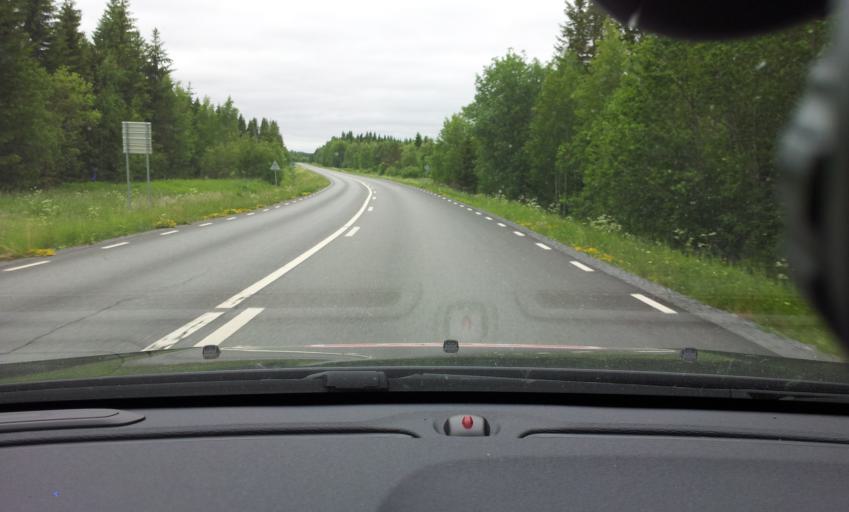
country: SE
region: Jaemtland
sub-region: Krokoms Kommun
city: Krokom
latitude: 63.0709
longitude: 14.3133
